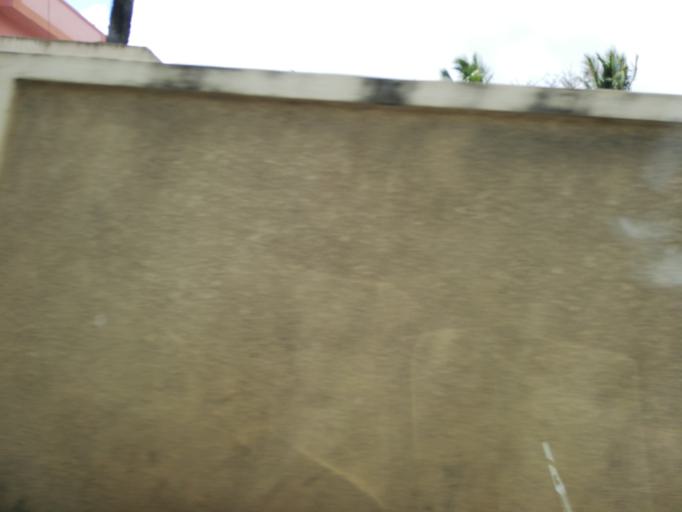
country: MU
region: Riviere du Rempart
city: Esperance Trebuchet
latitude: -20.0755
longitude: 57.6478
